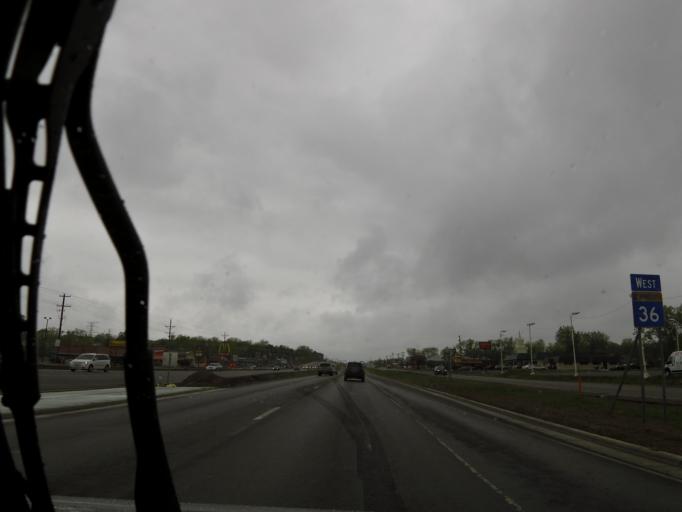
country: US
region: Minnesota
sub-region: Washington County
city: Oak Park Heights
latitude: 45.0360
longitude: -92.8086
